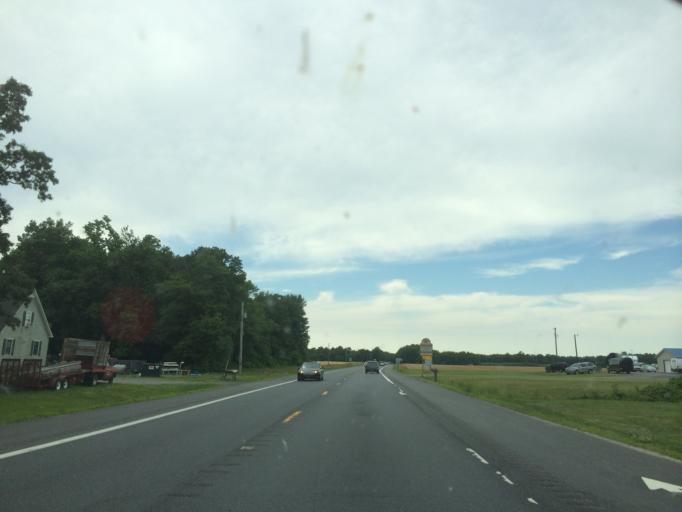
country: US
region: Maryland
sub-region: Caroline County
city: Federalsburg
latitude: 38.8018
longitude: -75.7204
